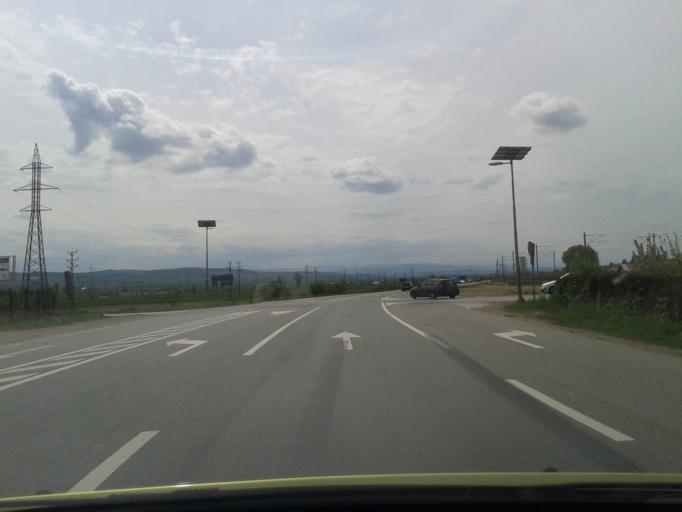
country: RO
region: Alba
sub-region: Municipiul Alba Iulia
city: Alba Iulia
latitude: 46.0727
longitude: 23.5962
